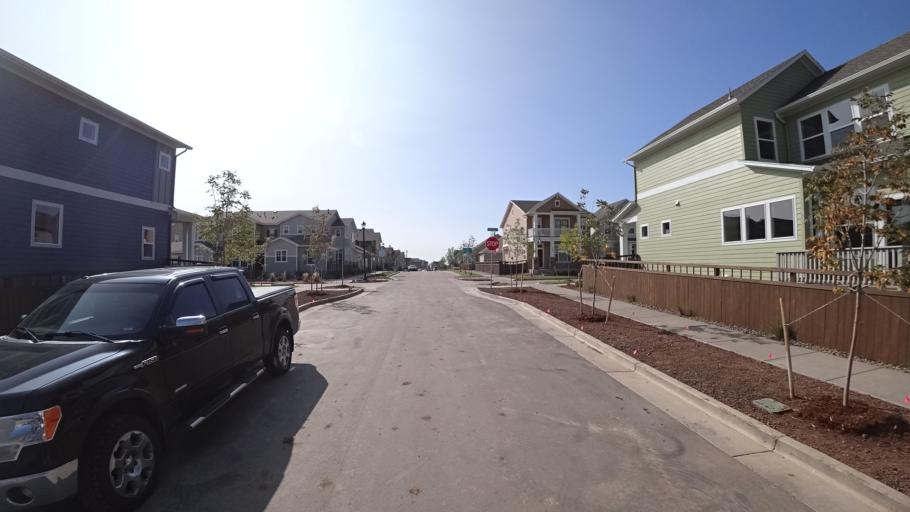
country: US
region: Colorado
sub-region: El Paso County
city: Colorado Springs
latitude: 38.8324
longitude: -104.8518
